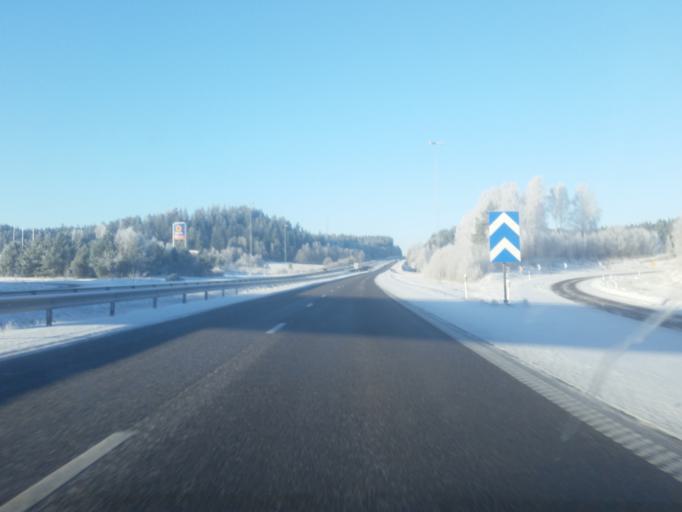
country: SE
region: Vaestra Goetaland
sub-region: Bollebygds Kommun
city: Bollebygd
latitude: 57.6633
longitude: 12.5451
